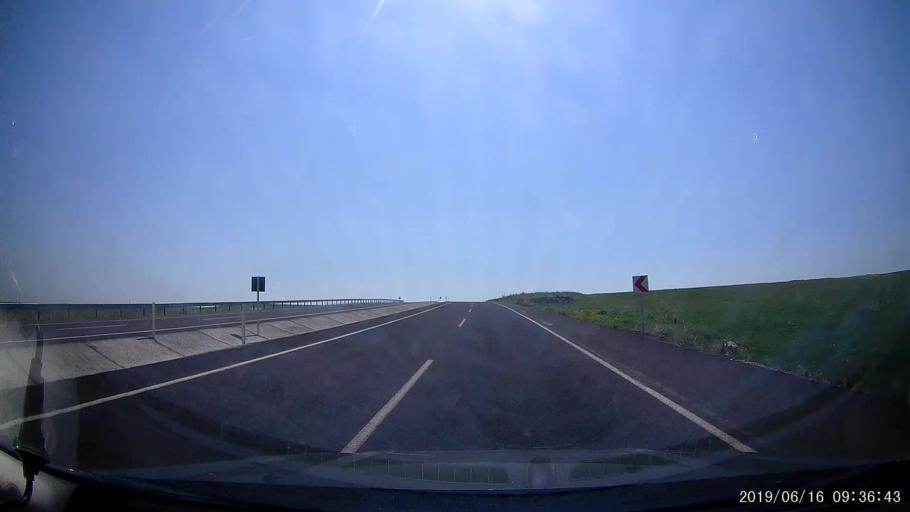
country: TR
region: Kars
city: Kars
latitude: 40.5561
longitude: 43.1785
